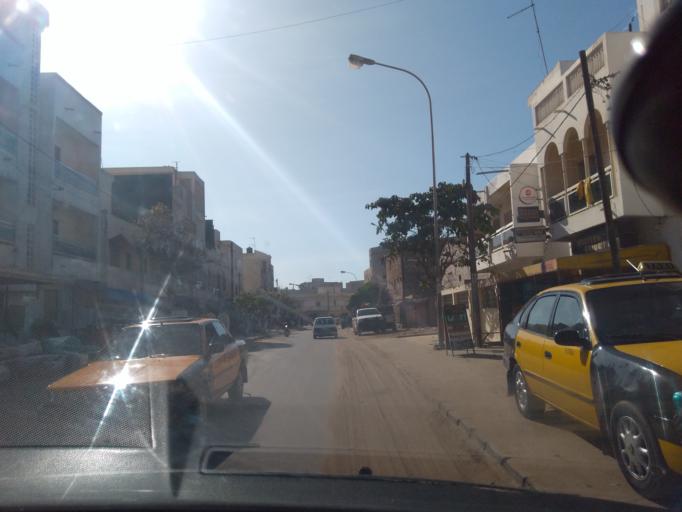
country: SN
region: Dakar
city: Pikine
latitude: 14.7595
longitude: -17.4324
